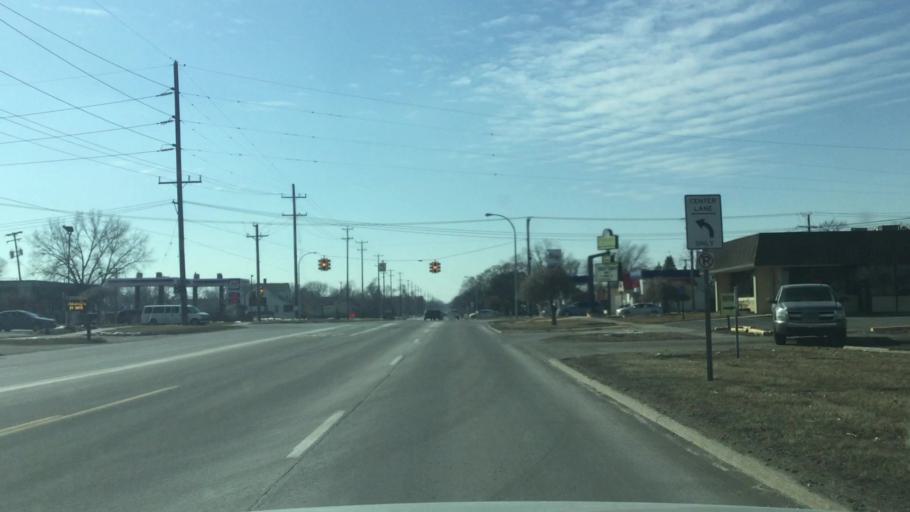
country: US
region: Michigan
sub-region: Wayne County
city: Garden City
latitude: 42.3105
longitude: -83.3635
